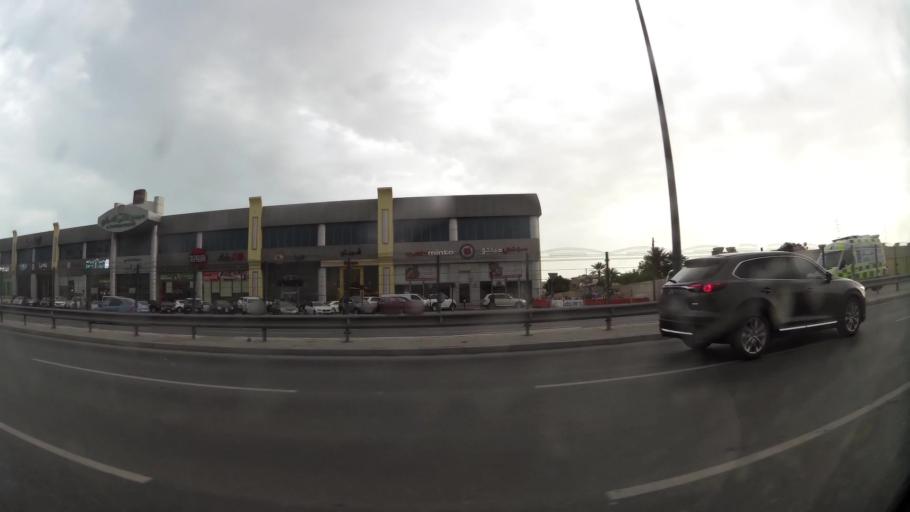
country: QA
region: Baladiyat ad Dawhah
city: Doha
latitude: 25.2705
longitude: 51.5075
